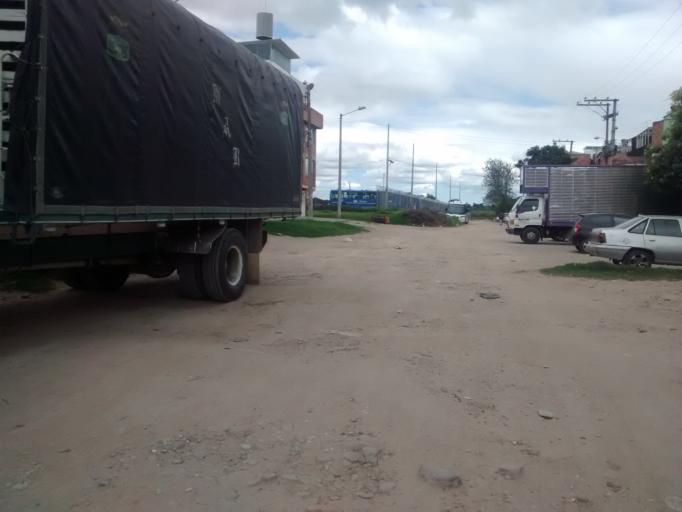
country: CO
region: Cundinamarca
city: Cota
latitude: 4.7187
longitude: -74.1023
